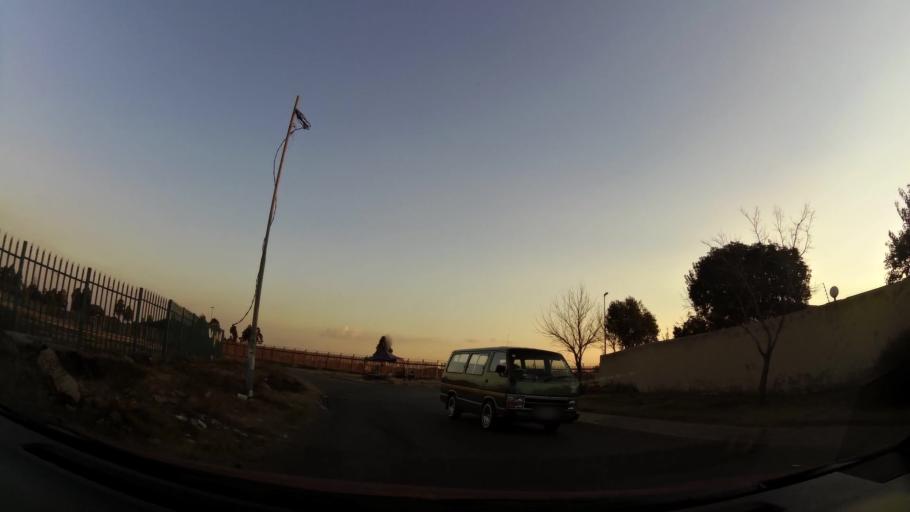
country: ZA
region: Gauteng
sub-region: City of Johannesburg Metropolitan Municipality
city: Soweto
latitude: -26.2262
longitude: 27.8451
